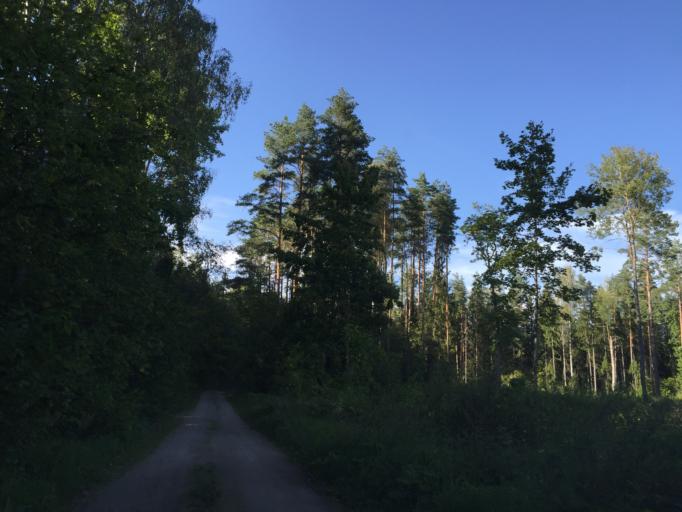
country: LT
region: Panevezys
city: Rokiskis
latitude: 55.8248
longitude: 25.8959
